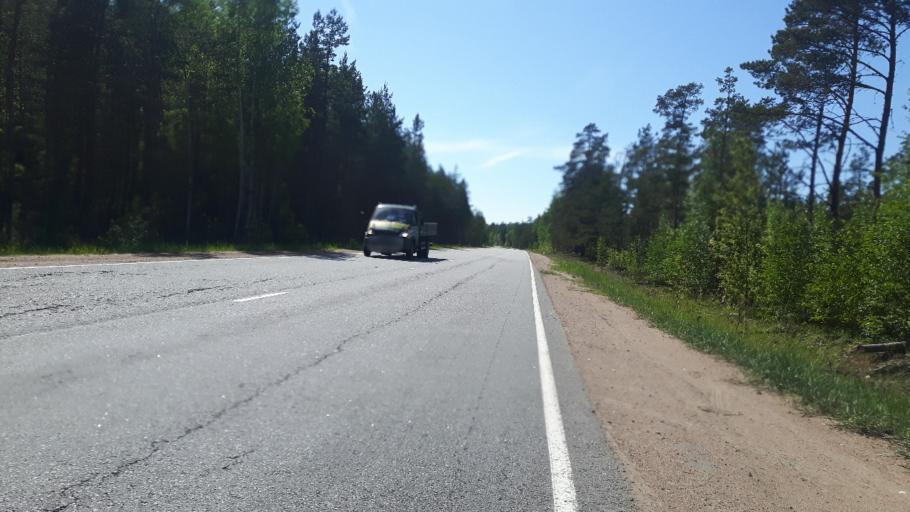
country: RU
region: Leningrad
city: Sista-Palkino
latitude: 59.7694
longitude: 28.7712
